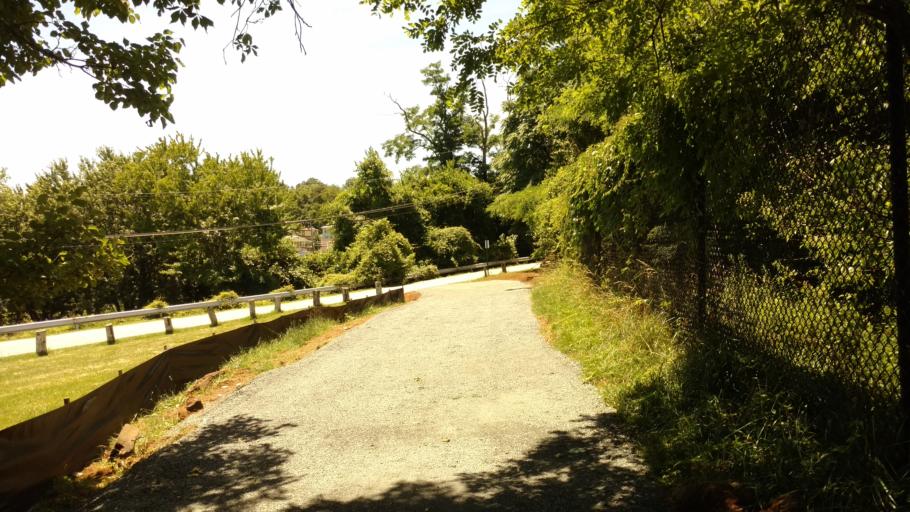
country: US
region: Maryland
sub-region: Baltimore County
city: Catonsville
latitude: 39.2642
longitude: -76.7271
